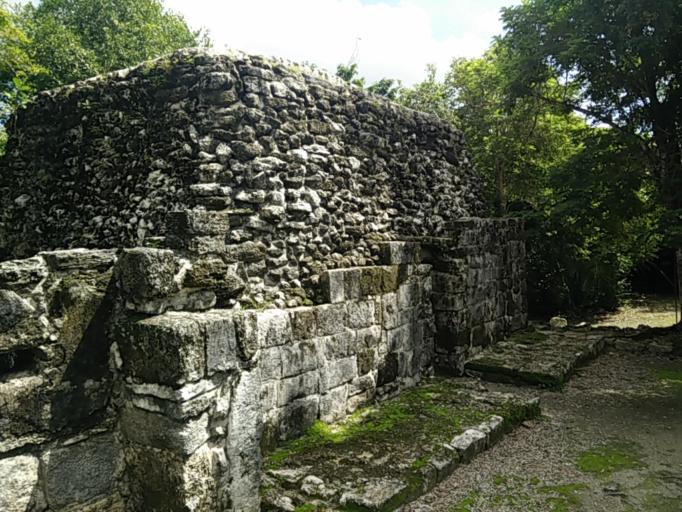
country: MX
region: Quintana Roo
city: San Miguel de Cozumel
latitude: 20.5039
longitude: -86.8462
